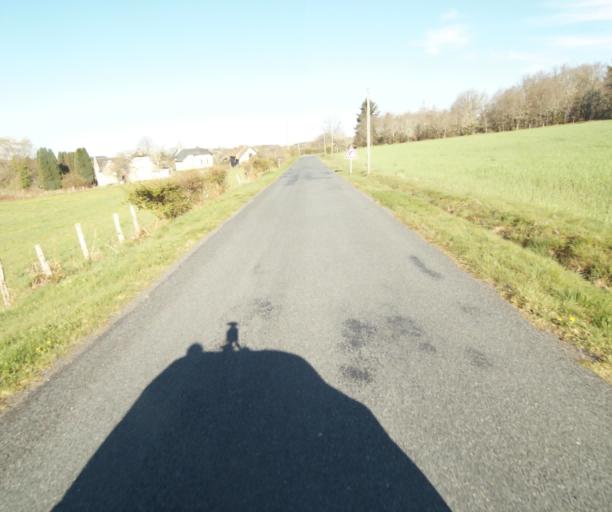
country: FR
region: Limousin
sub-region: Departement de la Correze
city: Correze
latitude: 45.3012
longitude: 1.8699
